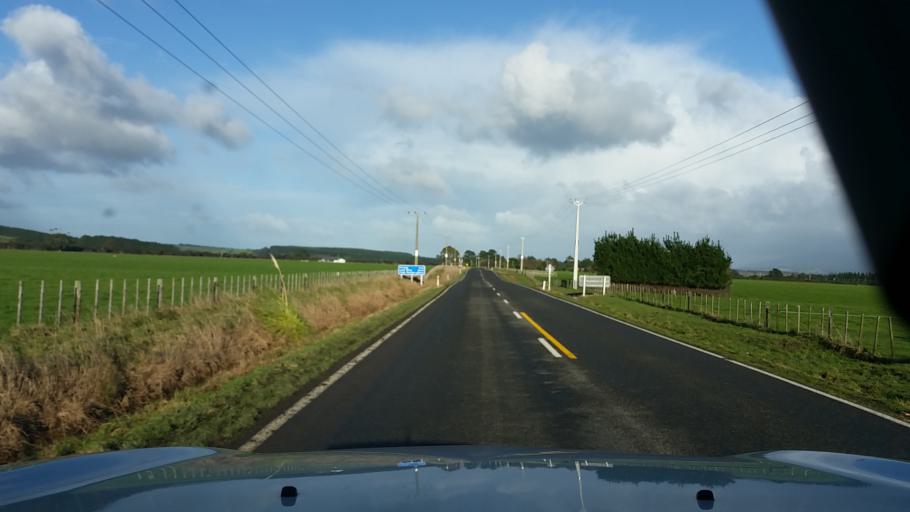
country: NZ
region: Wellington
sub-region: South Wairarapa District
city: Waipawa
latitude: -41.3066
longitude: 175.2728
